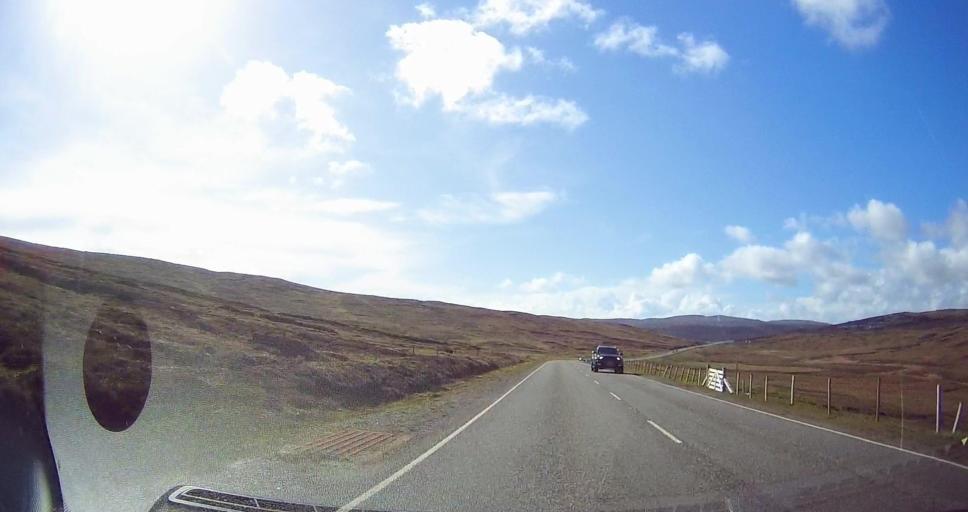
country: GB
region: Scotland
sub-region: Shetland Islands
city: Lerwick
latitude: 60.2668
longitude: -1.2265
